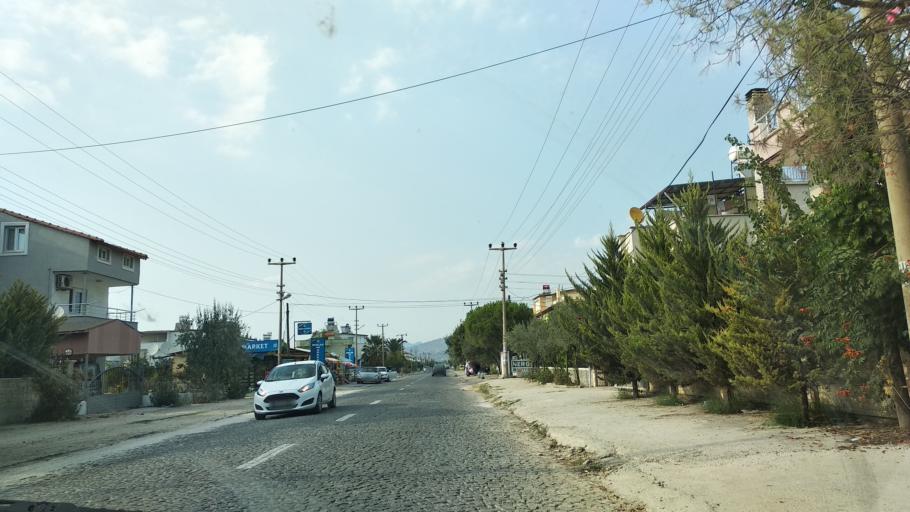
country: TR
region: Izmir
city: Dikili
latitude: 39.0983
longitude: 26.8828
